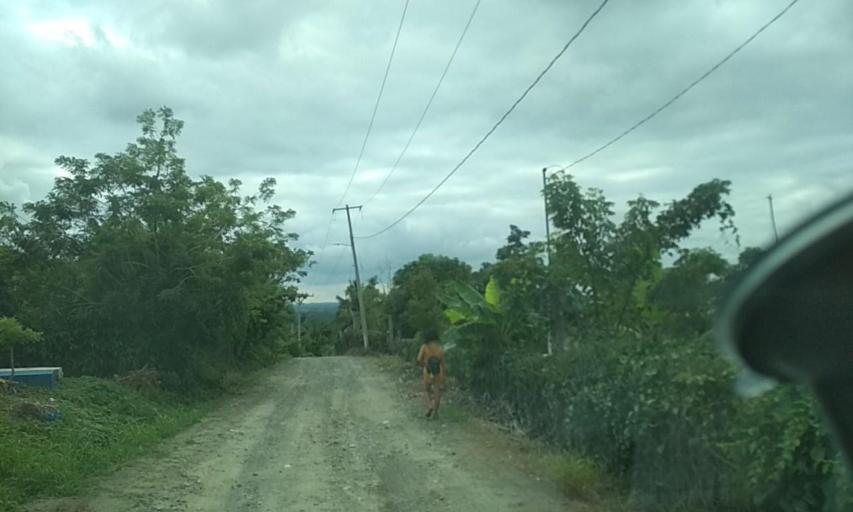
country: MX
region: Veracruz
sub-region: Papantla
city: Polutla
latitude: 20.5855
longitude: -97.2642
